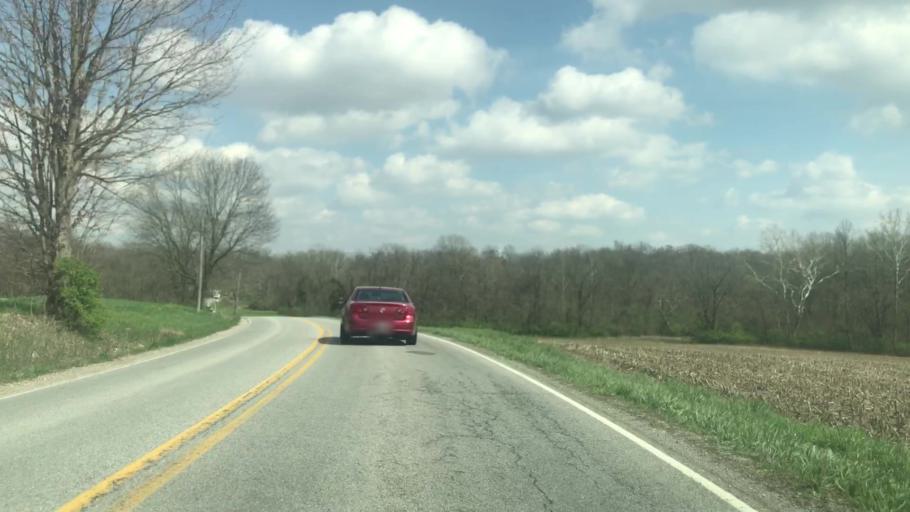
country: US
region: Indiana
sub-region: Johnson County
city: Waterloo
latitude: 39.5527
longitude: -86.2156
